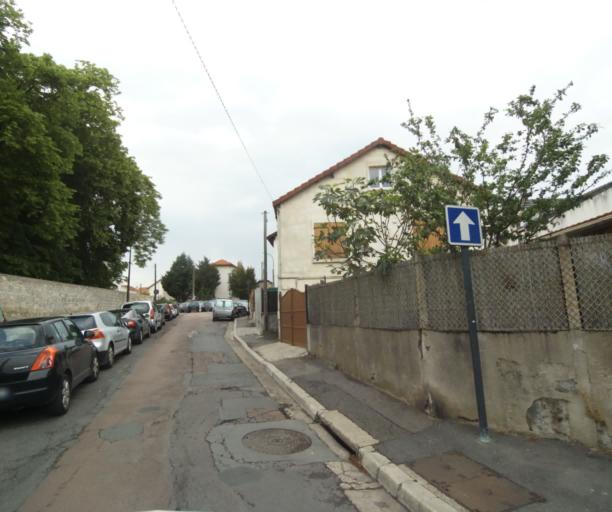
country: FR
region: Ile-de-France
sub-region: Departement du Val-d'Oise
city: Argenteuil
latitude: 48.9409
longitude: 2.2370
